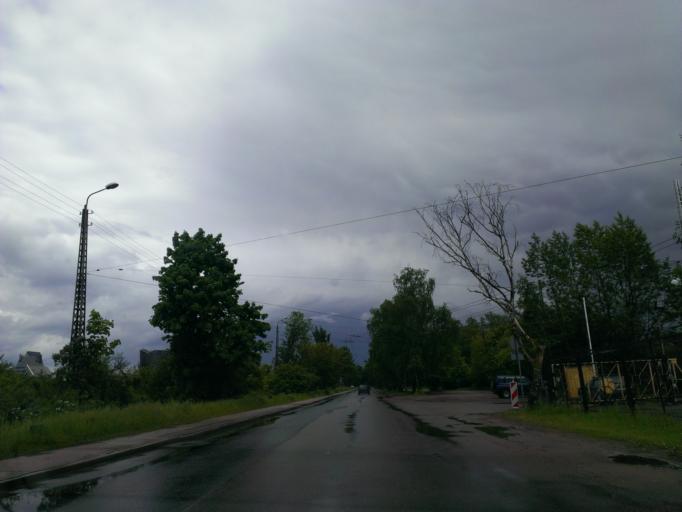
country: LV
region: Riga
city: Riga
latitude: 56.9332
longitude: 24.0946
